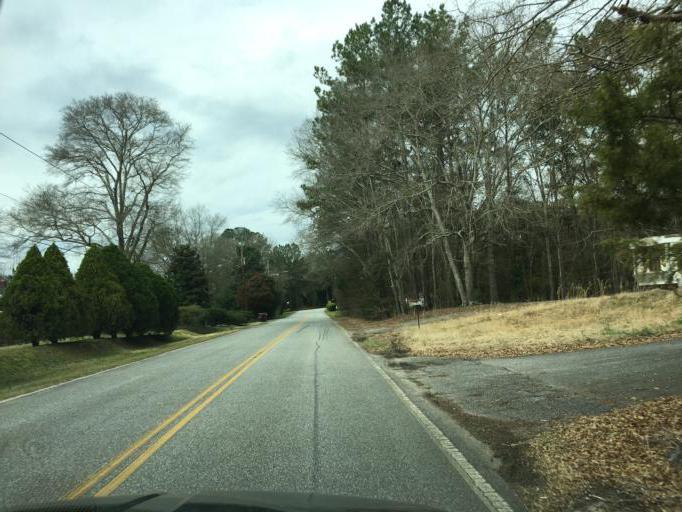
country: US
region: South Carolina
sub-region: Anderson County
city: Pendleton
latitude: 34.6584
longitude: -82.7851
